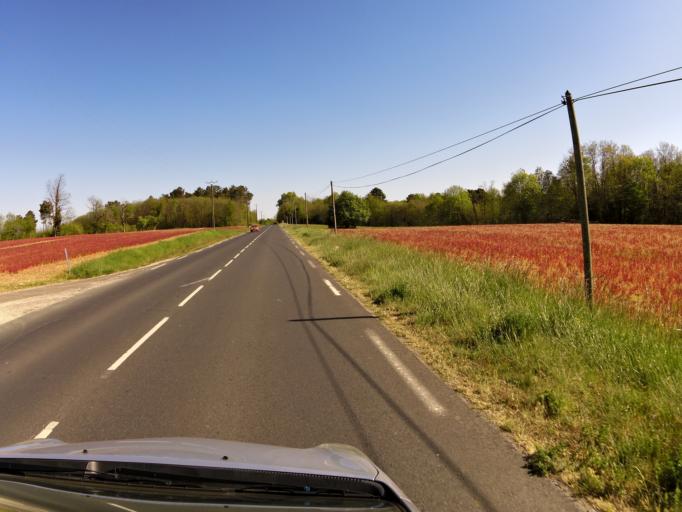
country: FR
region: Aquitaine
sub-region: Departement de la Dordogne
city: Montignac
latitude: 45.0162
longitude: 1.2369
